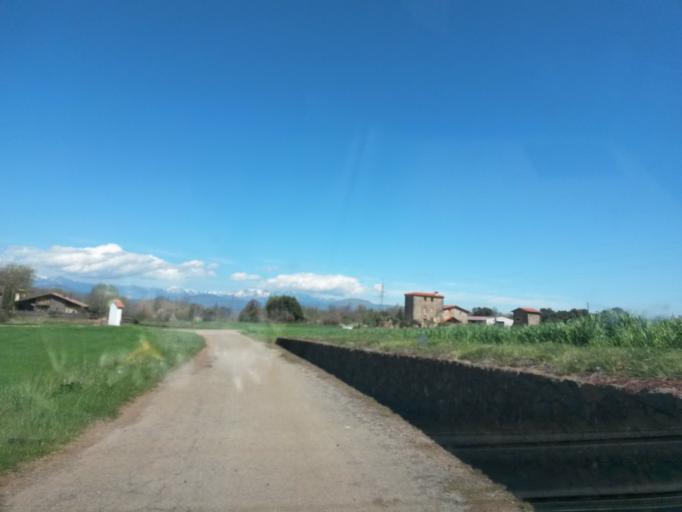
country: ES
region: Catalonia
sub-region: Provincia de Girona
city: Sant Cristofol de les Fonts
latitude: 42.1719
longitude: 2.5319
